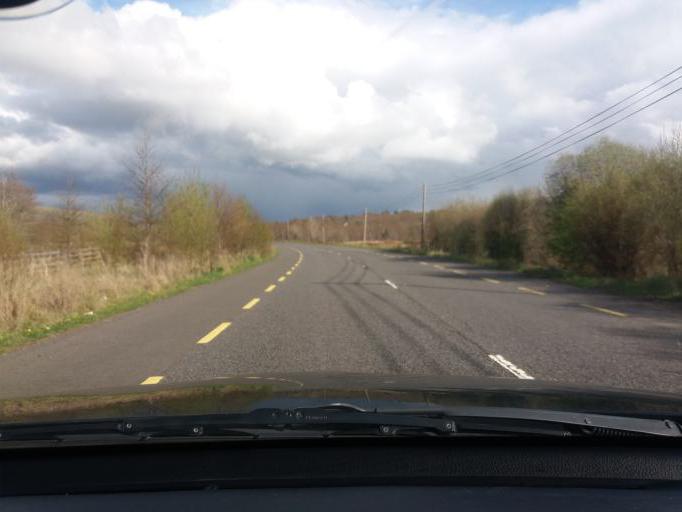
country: IE
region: Connaught
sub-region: County Leitrim
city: Manorhamilton
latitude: 54.3500
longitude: -8.2448
